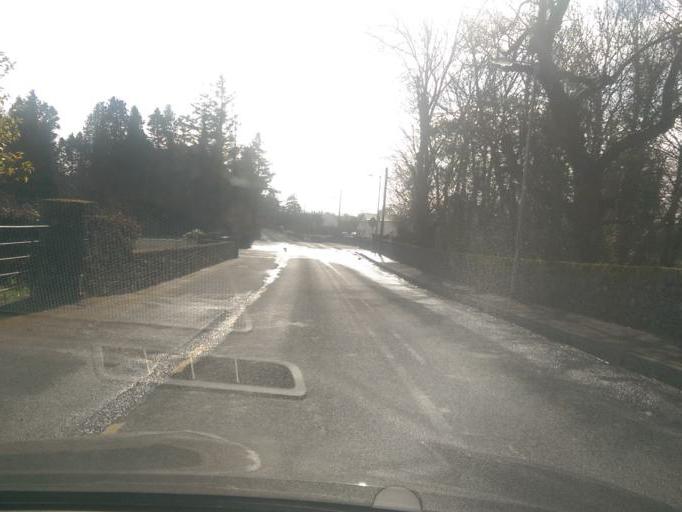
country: IE
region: Connaught
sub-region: County Galway
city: Athenry
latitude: 53.3734
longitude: -8.7012
